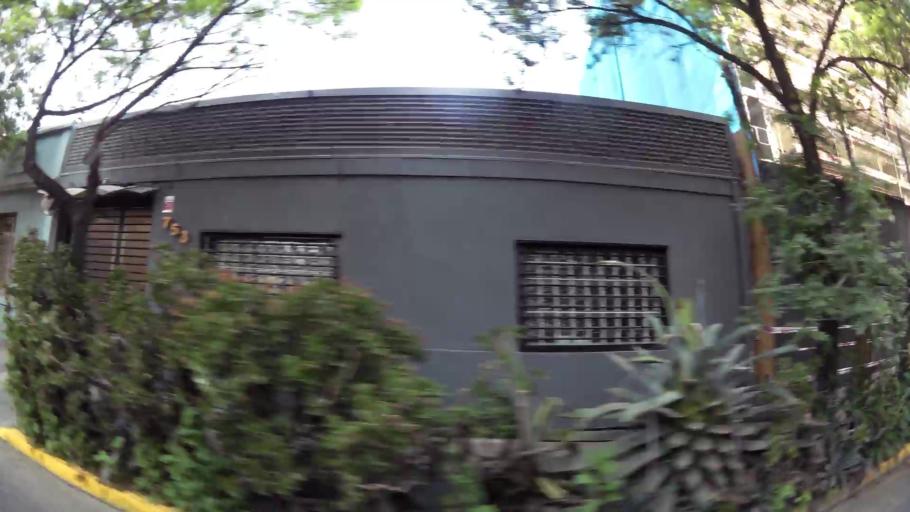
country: CL
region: Santiago Metropolitan
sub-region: Provincia de Santiago
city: Santiago
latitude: -33.4476
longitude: -70.6205
